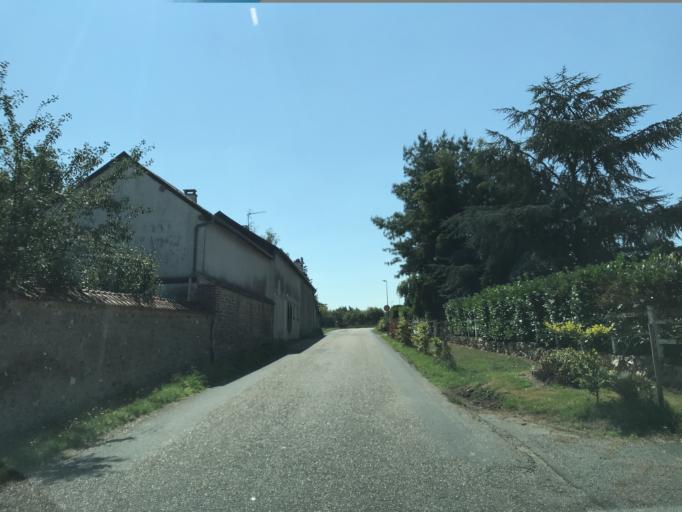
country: FR
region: Haute-Normandie
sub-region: Departement de l'Eure
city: Heudreville-sur-Eure
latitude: 49.0970
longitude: 1.2083
